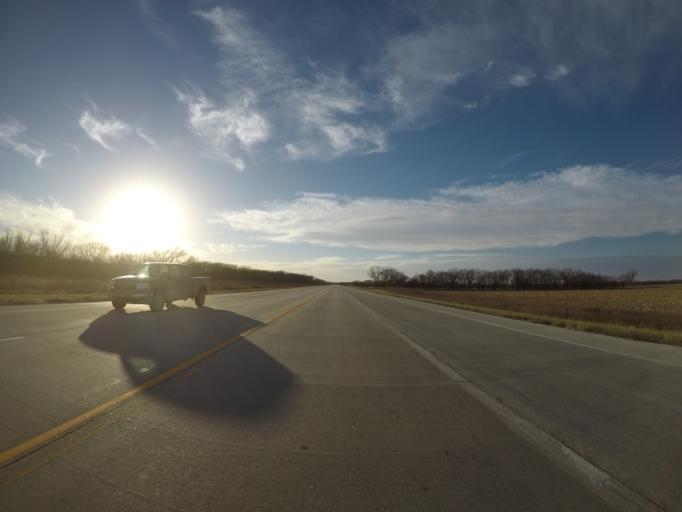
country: US
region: Kansas
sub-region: Lyon County
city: Emporia
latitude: 38.4068
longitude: -96.3614
